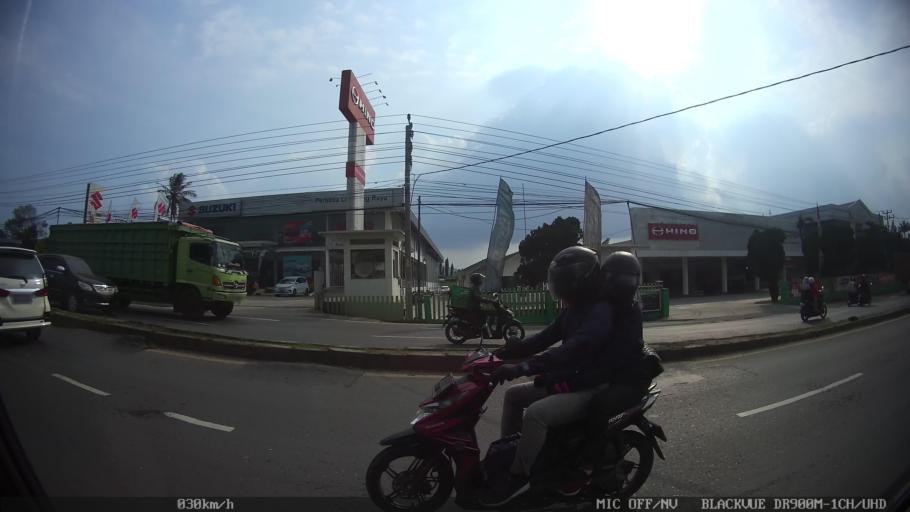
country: ID
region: Lampung
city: Kedaton
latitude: -5.3551
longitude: 105.2205
